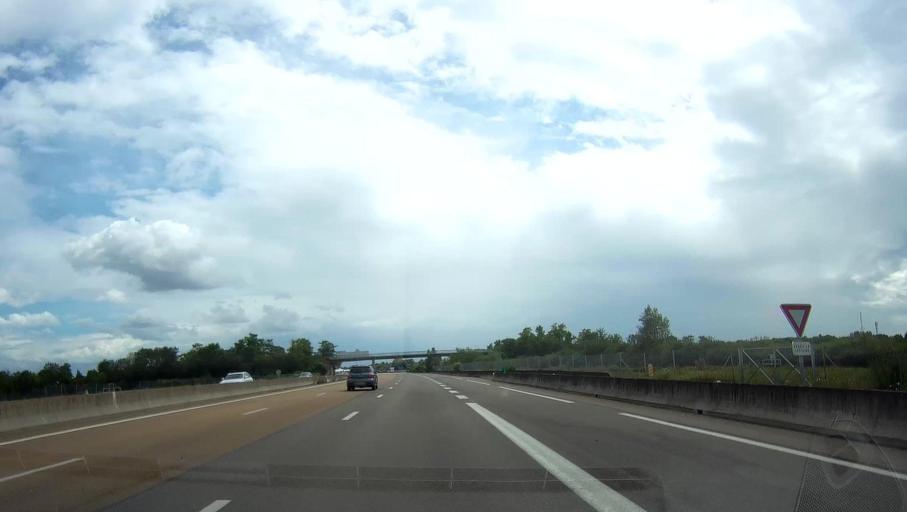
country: FR
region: Bourgogne
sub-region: Departement de la Cote-d'Or
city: Couternon
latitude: 47.3430
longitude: 5.1641
